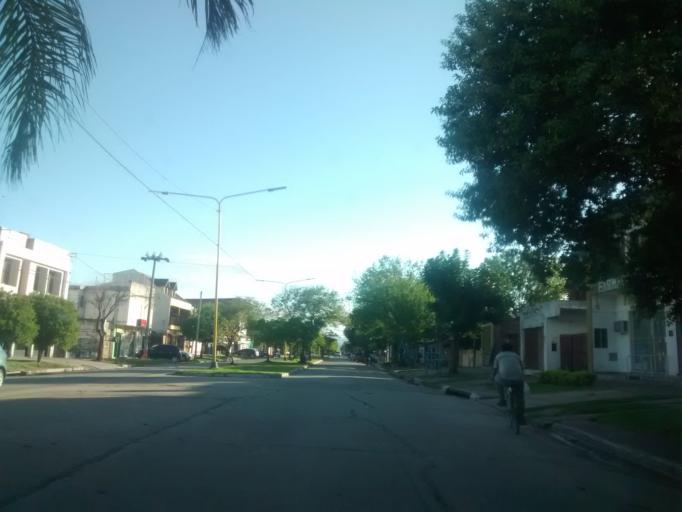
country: AR
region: Chaco
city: Resistencia
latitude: -27.4606
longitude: -58.9970
